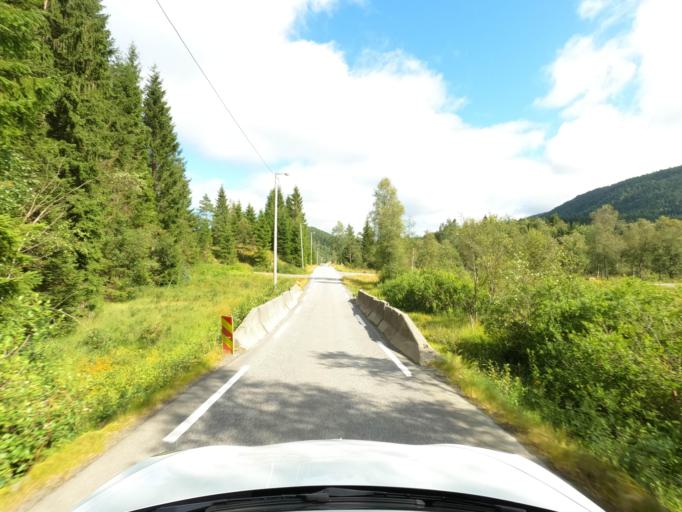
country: NO
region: Hordaland
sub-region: Os
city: Syfteland
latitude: 60.2964
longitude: 5.4431
